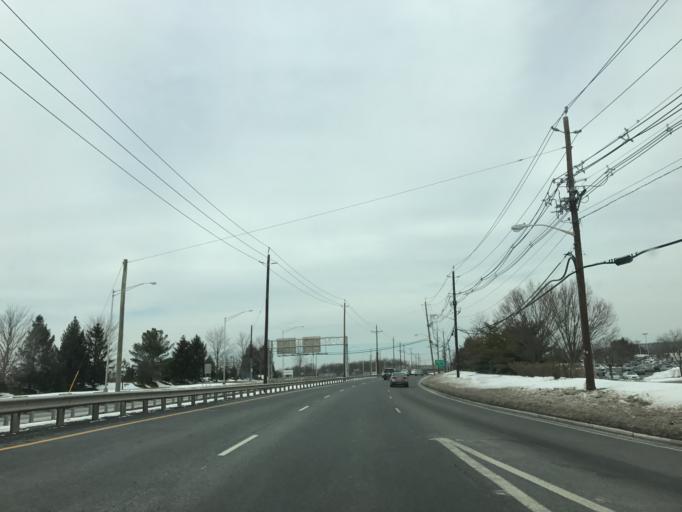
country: US
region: New Jersey
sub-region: Somerset County
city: Somerville
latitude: 40.5851
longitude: -74.6221
